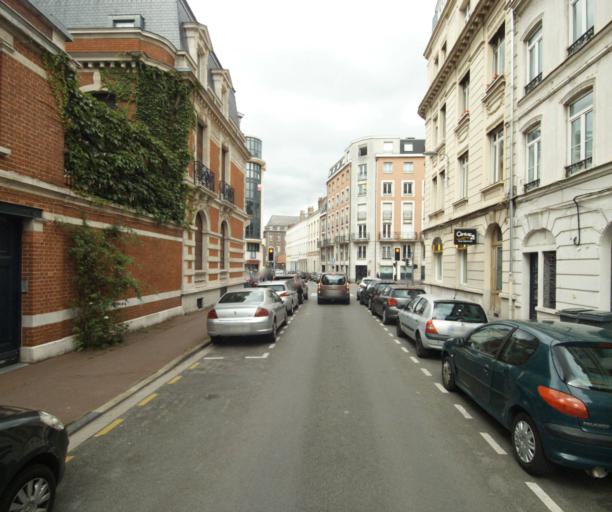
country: FR
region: Nord-Pas-de-Calais
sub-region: Departement du Nord
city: Lille
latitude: 50.6319
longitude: 3.0513
